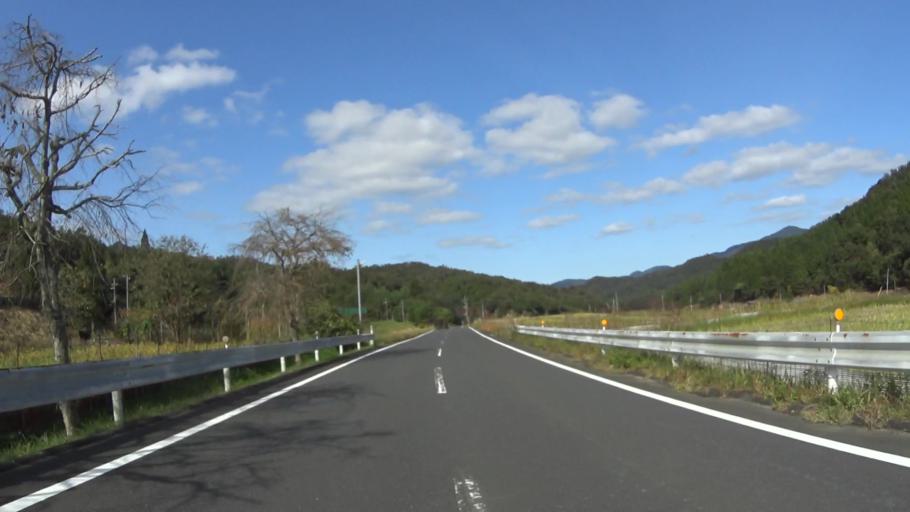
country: JP
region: Hyogo
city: Toyooka
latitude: 35.5496
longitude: 134.9775
